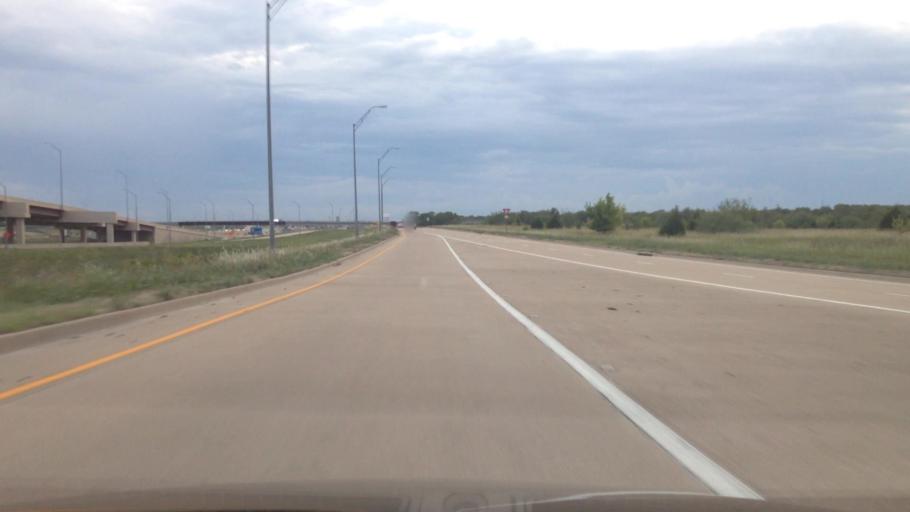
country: US
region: Texas
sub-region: Tarrant County
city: Grapevine
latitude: 32.9337
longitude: -97.0437
